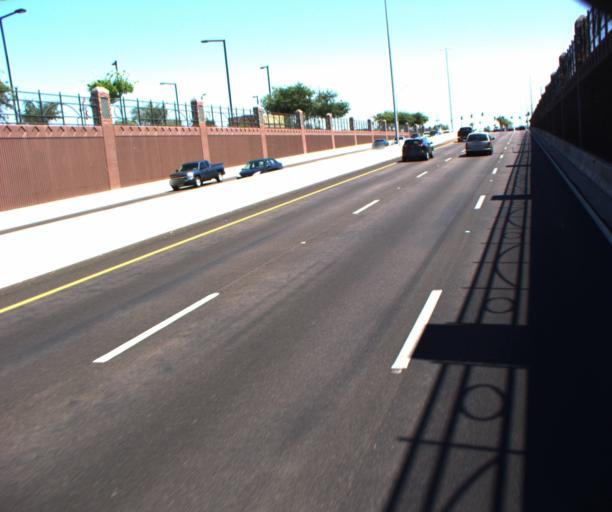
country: US
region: Arizona
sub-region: Maricopa County
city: Glendale
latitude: 33.5376
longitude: -112.1850
